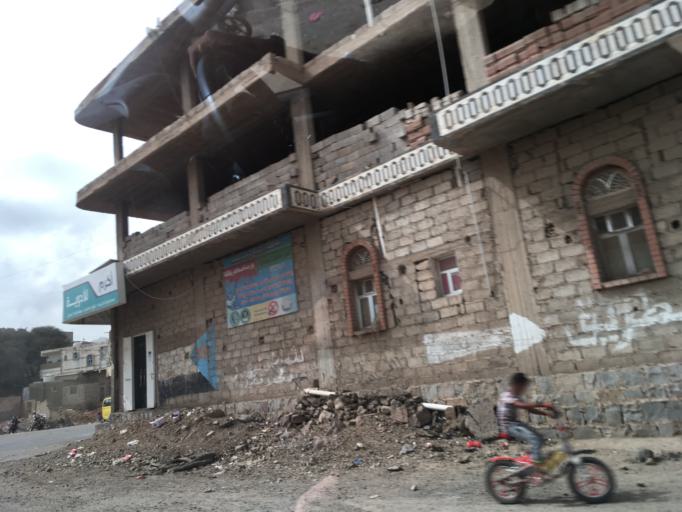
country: YE
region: Ad Dali'
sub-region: Ad Dhale'e
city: Dhalie
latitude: 13.6970
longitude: 44.7293
